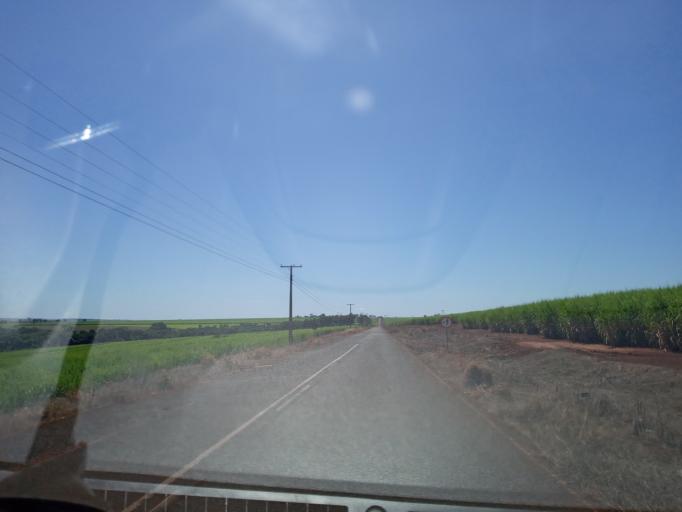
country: BR
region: Goias
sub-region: Itumbiara
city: Itumbiara
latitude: -18.4241
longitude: -49.1637
